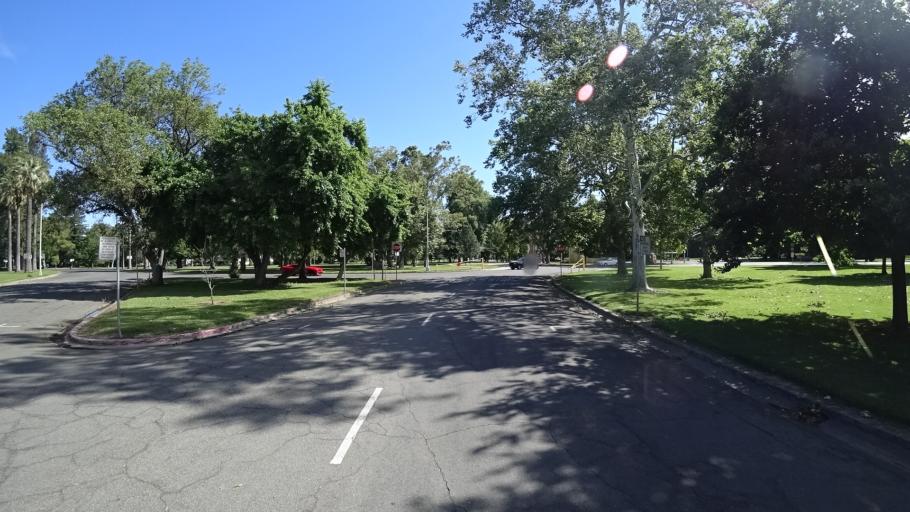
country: US
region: California
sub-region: Sacramento County
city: Sacramento
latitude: 38.5405
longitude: -121.4931
